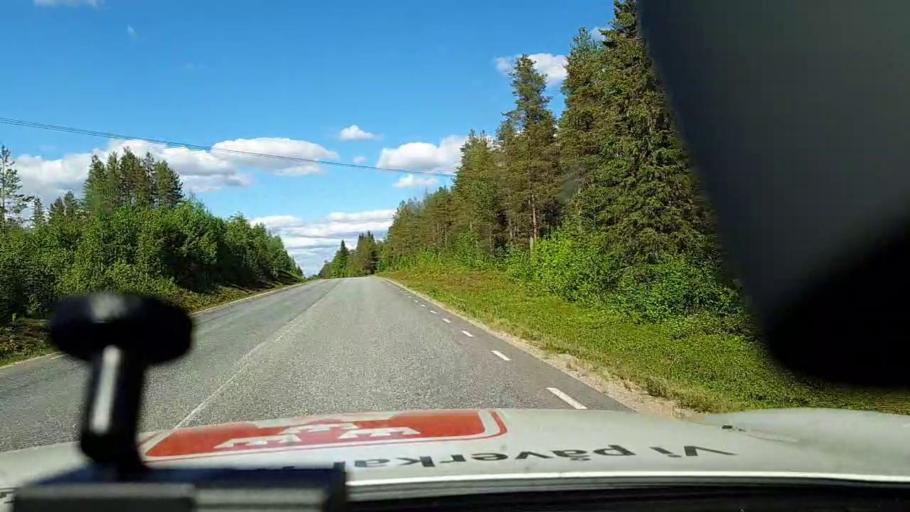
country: FI
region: Lapland
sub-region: Torniolaakso
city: Ylitornio
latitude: 66.3299
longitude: 23.6328
